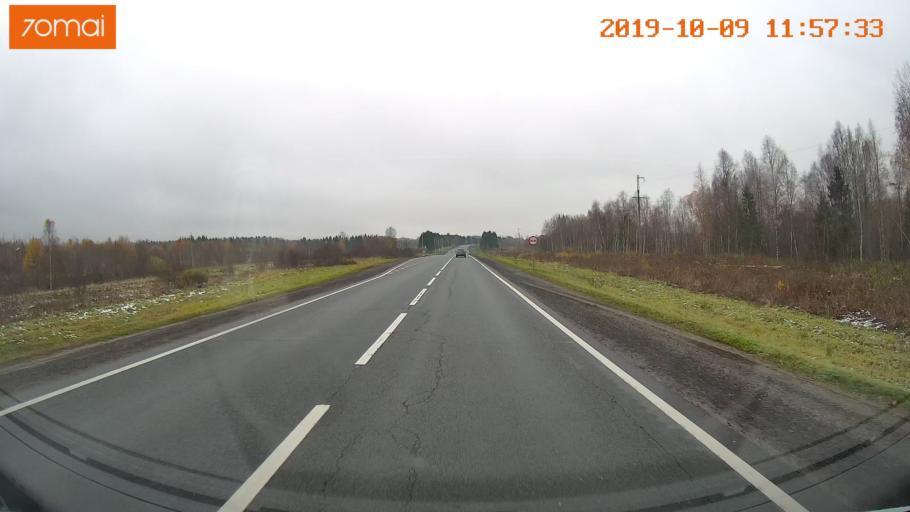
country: RU
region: Vologda
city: Gryazovets
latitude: 58.7306
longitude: 40.2933
